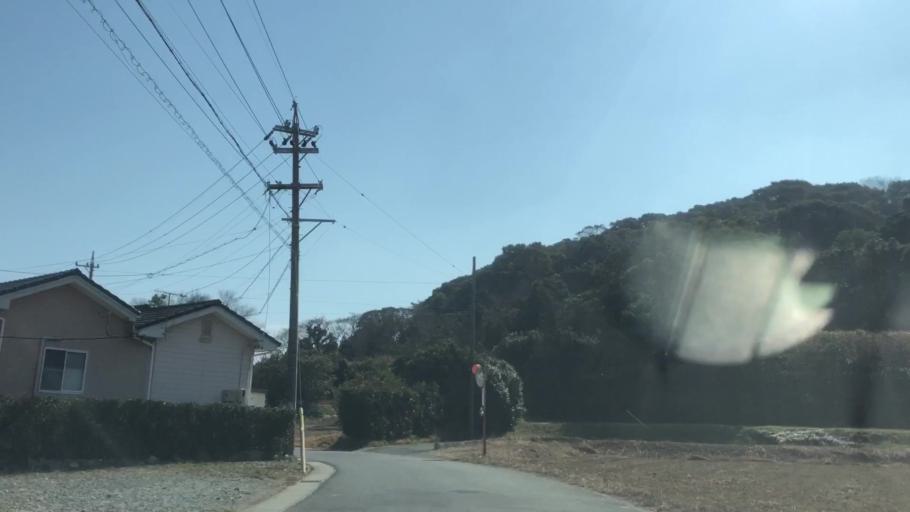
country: JP
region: Aichi
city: Tahara
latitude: 34.6681
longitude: 137.2548
